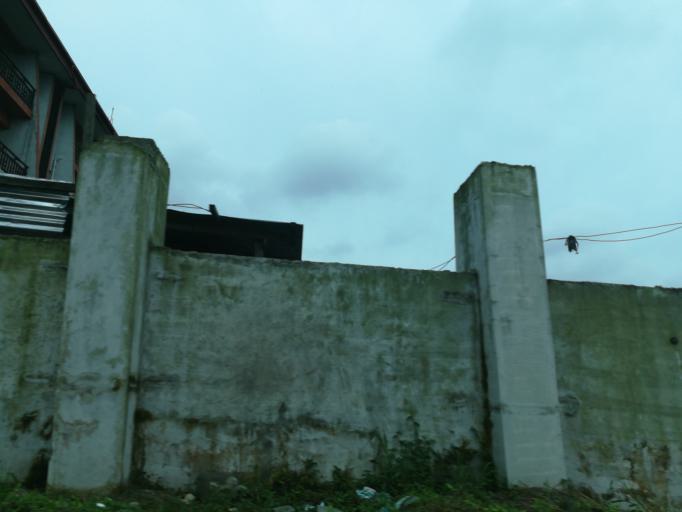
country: NG
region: Rivers
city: Port Harcourt
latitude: 4.8142
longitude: 6.9941
